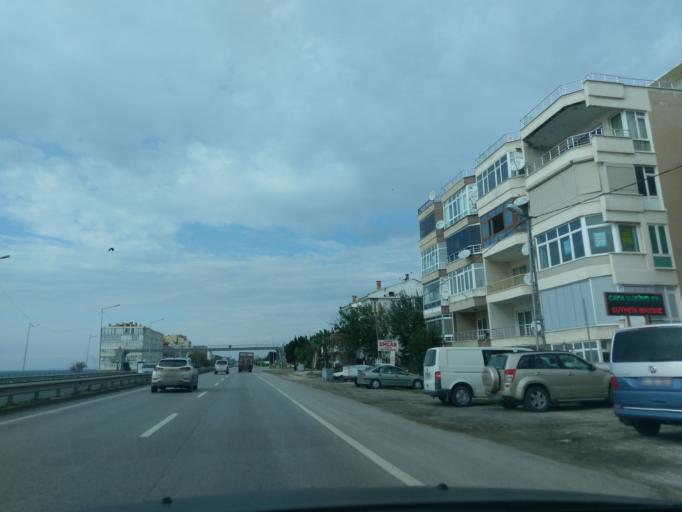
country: TR
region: Istanbul
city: Celaliye
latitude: 41.0453
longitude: 28.4091
